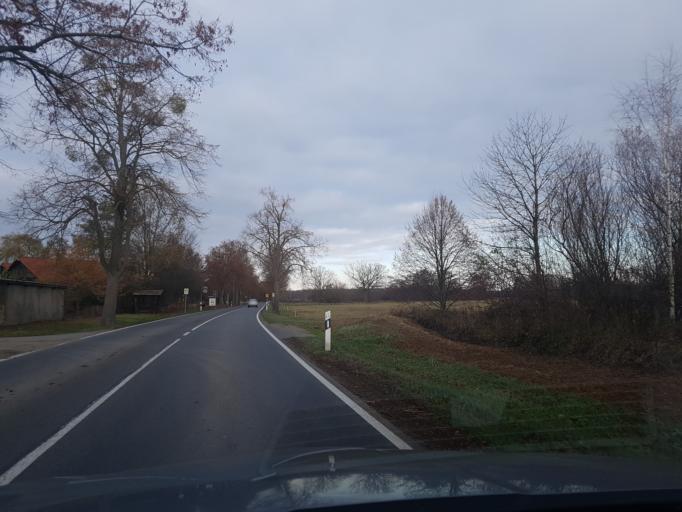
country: DE
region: Brandenburg
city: Golssen
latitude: 51.9654
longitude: 13.6159
